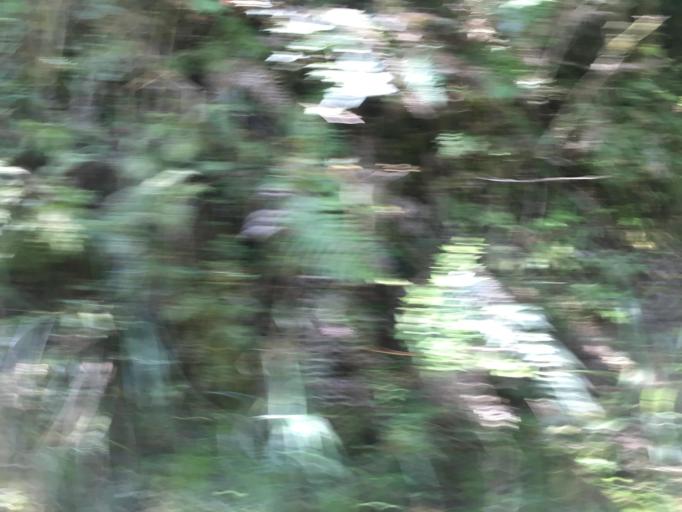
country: TW
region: Taiwan
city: Daxi
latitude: 24.6078
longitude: 121.4595
